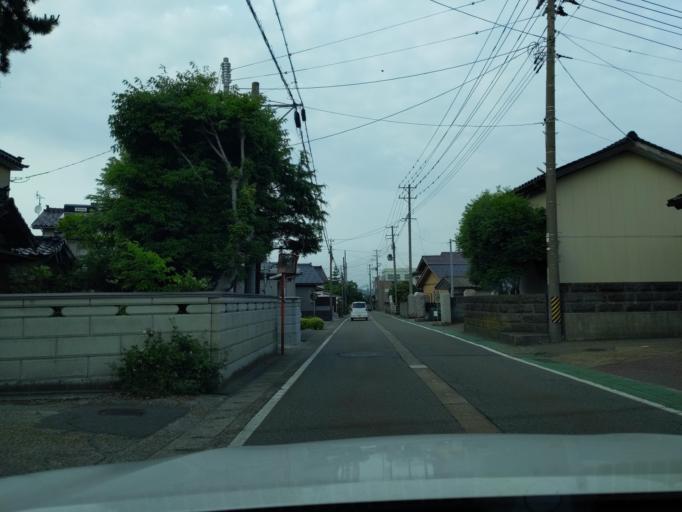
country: JP
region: Niigata
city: Kashiwazaki
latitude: 37.3799
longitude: 138.5706
